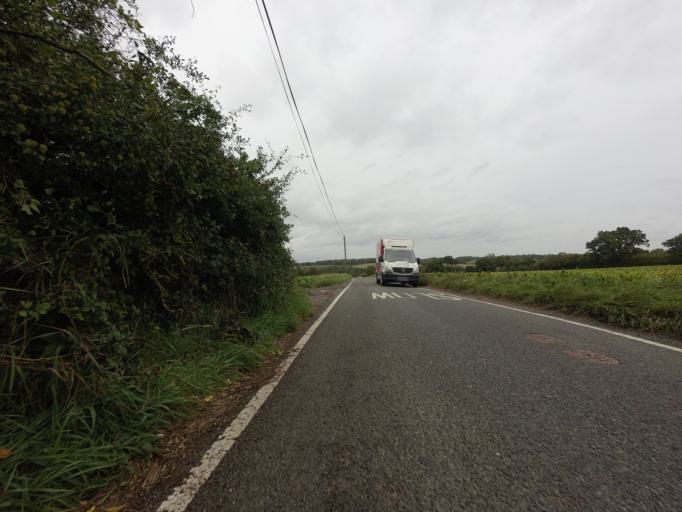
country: GB
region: England
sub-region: Cambridgeshire
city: Duxford
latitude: 52.0138
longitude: 0.1250
